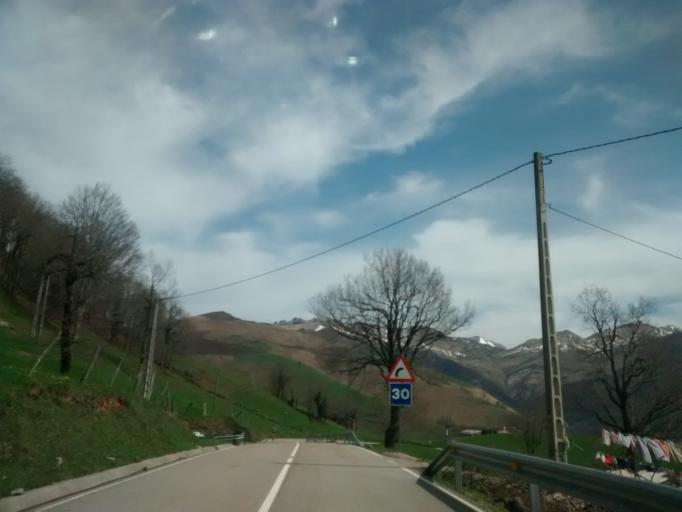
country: ES
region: Cantabria
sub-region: Provincia de Cantabria
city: Vega de Pas
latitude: 43.1669
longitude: -3.7763
